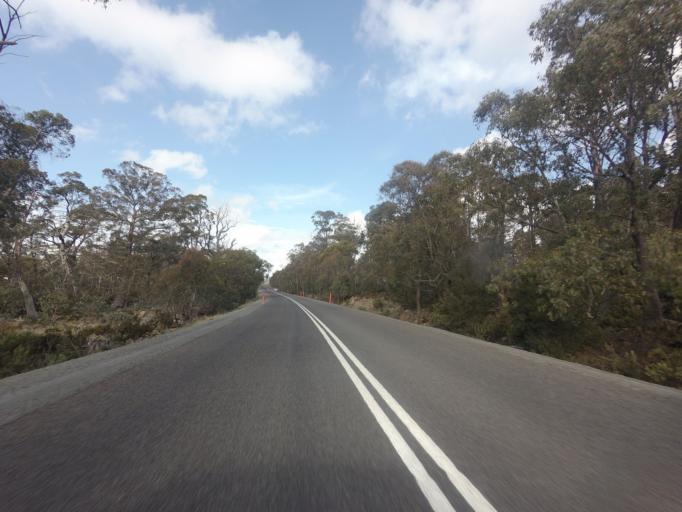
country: AU
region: Tasmania
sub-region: Meander Valley
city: Deloraine
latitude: -41.8413
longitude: 146.6841
